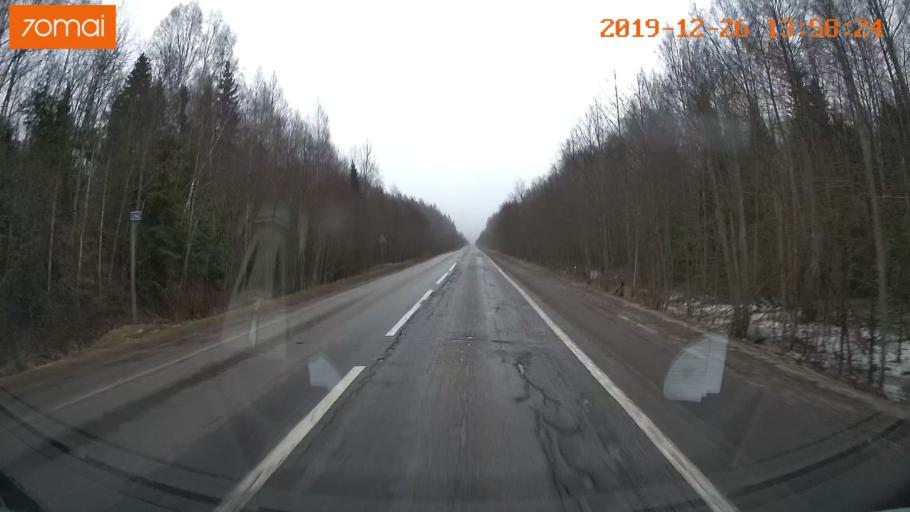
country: RU
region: Jaroslavl
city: Poshekhon'ye
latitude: 58.5745
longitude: 38.6999
